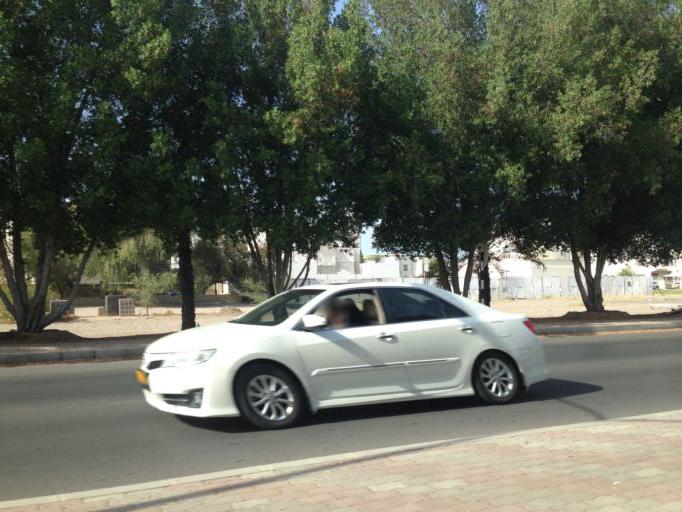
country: OM
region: Muhafazat Masqat
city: As Sib al Jadidah
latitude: 23.6138
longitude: 58.2251
